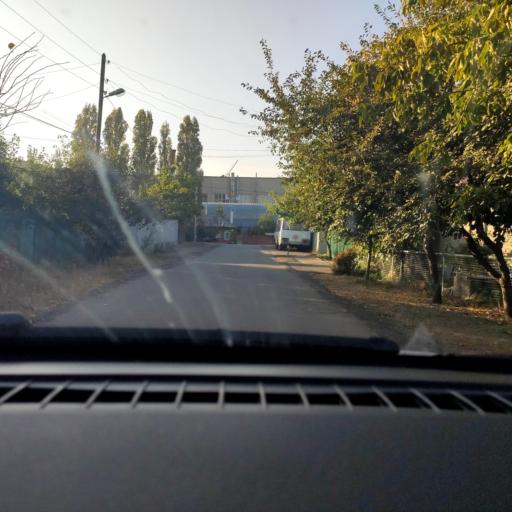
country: RU
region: Voronezj
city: Voronezh
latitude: 51.6700
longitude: 39.2645
